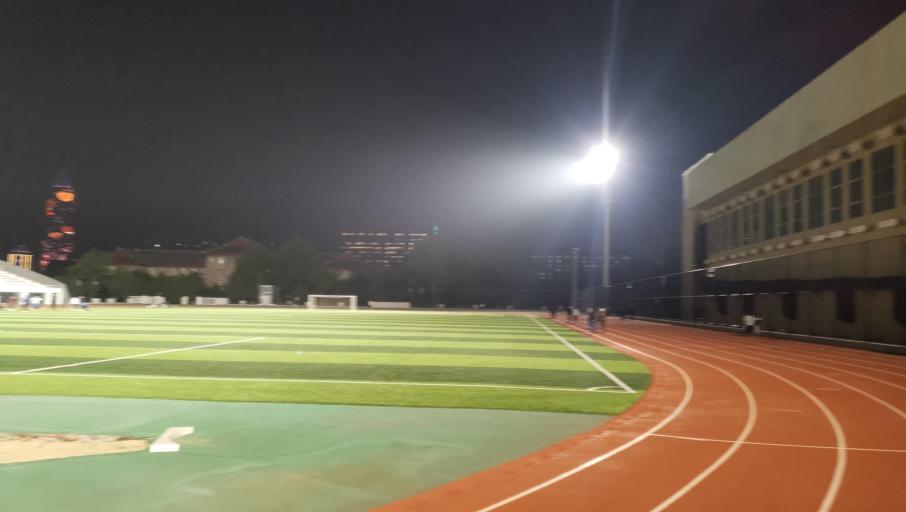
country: CN
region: Shandong Sheng
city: Jinan
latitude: 36.6499
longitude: 117.0131
